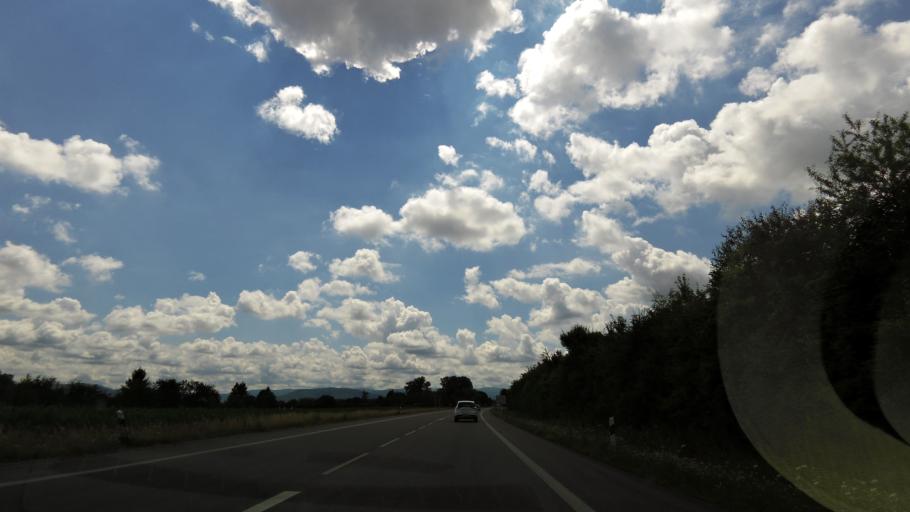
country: DE
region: Baden-Wuerttemberg
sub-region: Karlsruhe Region
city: Iffezheim
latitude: 48.8264
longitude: 8.1263
